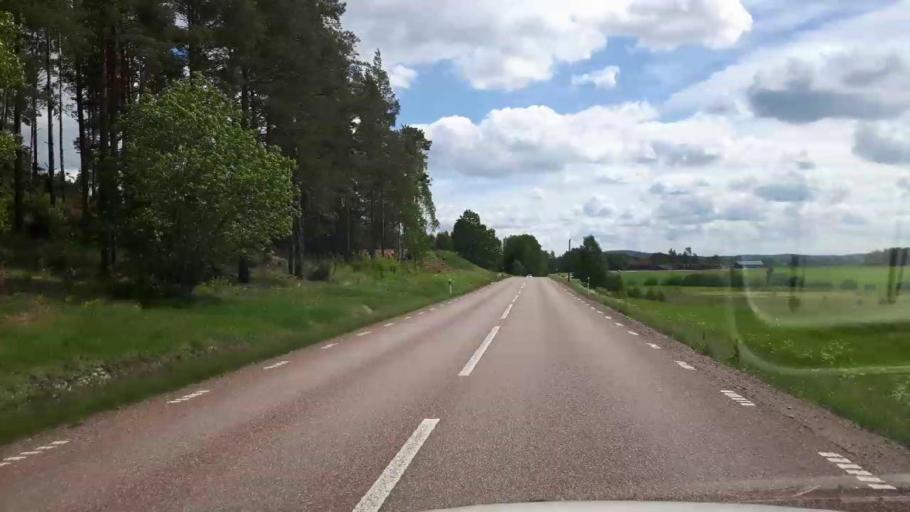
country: SE
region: Dalarna
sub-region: Saters Kommun
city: Saeter
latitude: 60.4078
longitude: 15.8639
